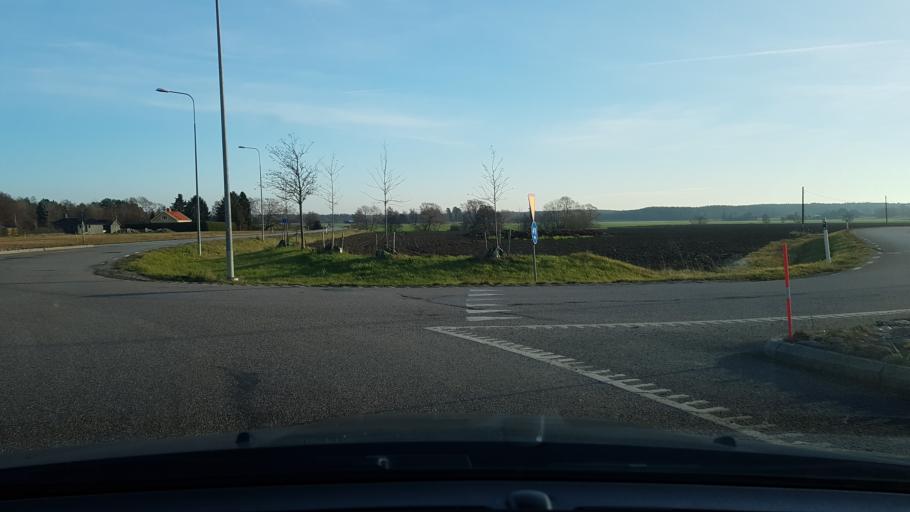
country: SE
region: Stockholm
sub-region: Vallentuna Kommun
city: Vallentuna
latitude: 59.7515
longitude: 18.0434
